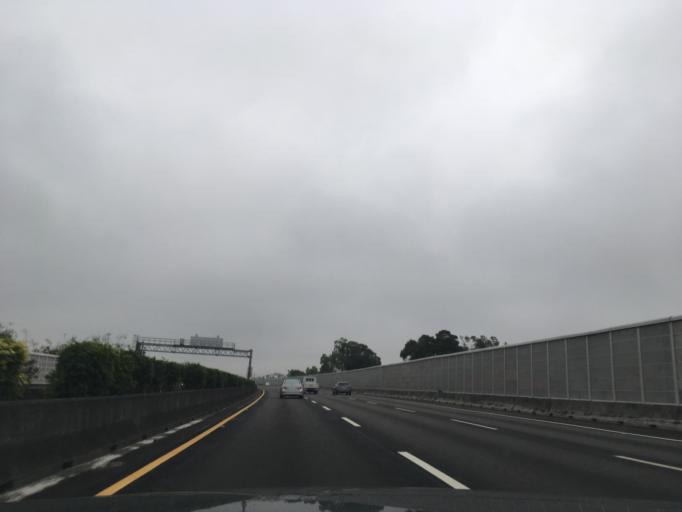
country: TW
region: Taiwan
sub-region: Miaoli
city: Miaoli
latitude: 24.5197
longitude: 120.8142
